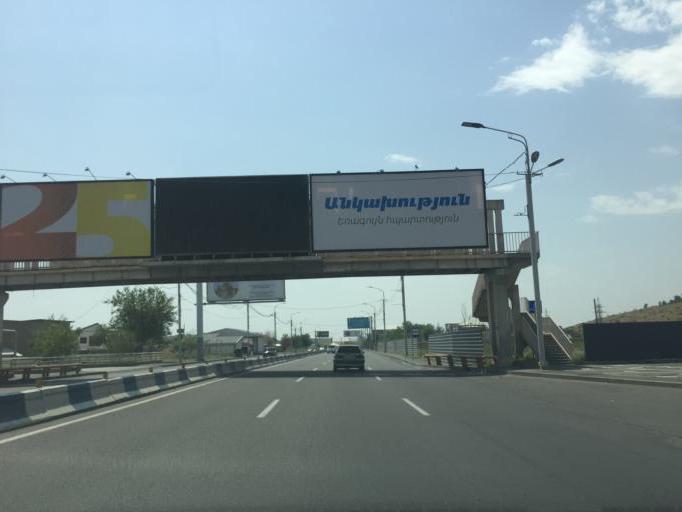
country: AM
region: Ararat
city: Argavand
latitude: 40.1578
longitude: 44.4622
